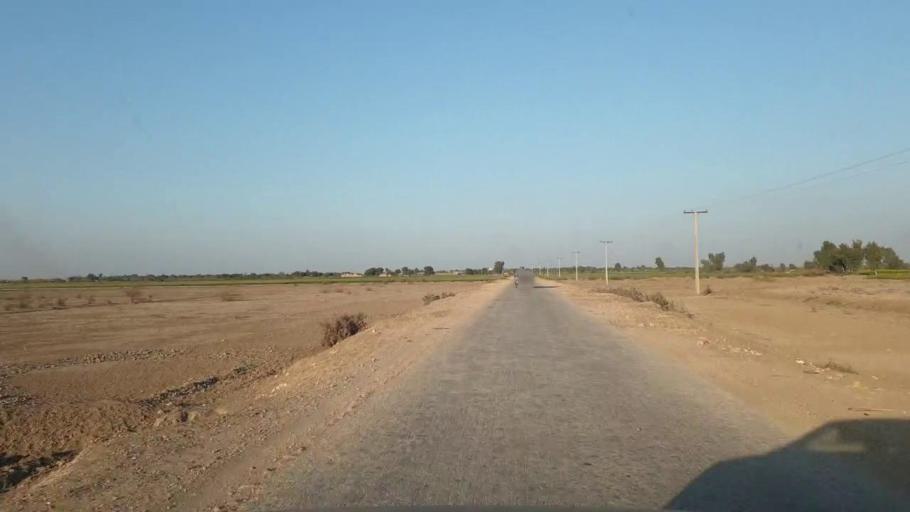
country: PK
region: Sindh
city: Tando Allahyar
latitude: 25.3812
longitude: 68.7515
